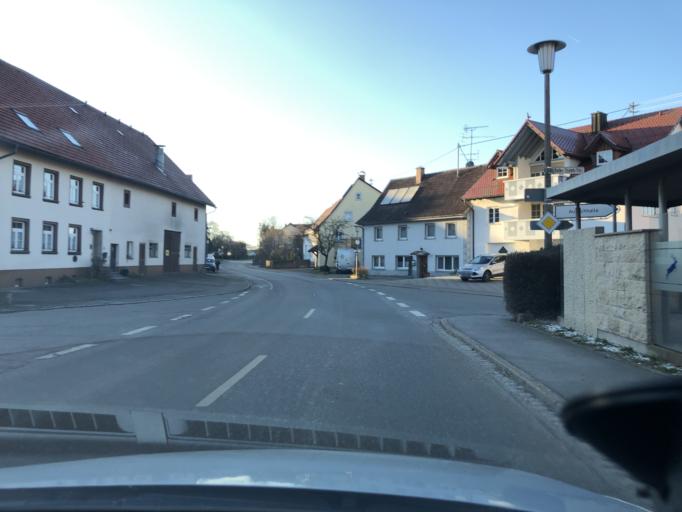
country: DE
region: Baden-Wuerttemberg
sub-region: Freiburg Region
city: Hufingen
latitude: 47.8703
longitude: 8.4644
